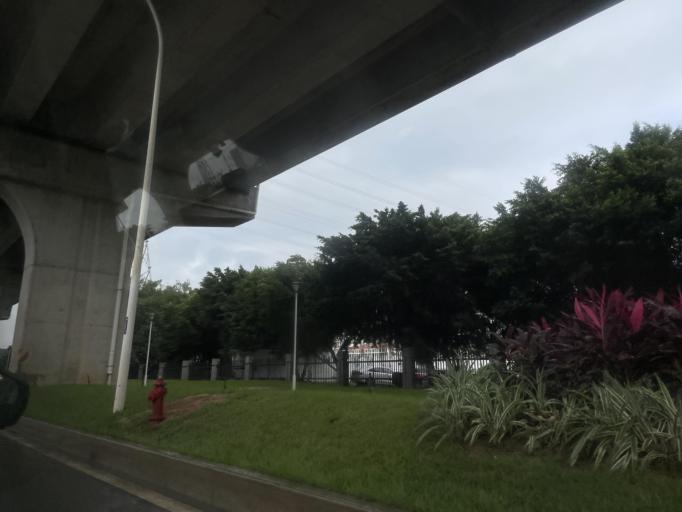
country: CN
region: Guangdong
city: Wanzai
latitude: 22.1766
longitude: 113.4908
